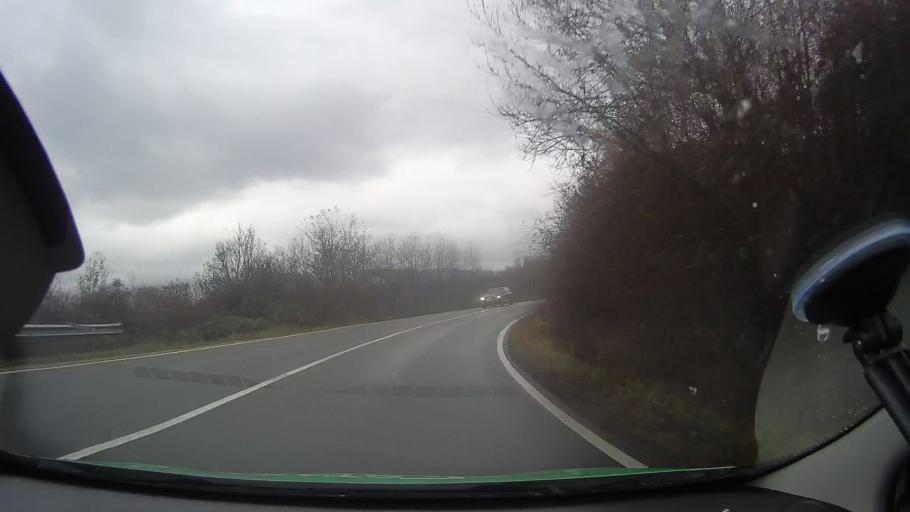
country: RO
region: Arad
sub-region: Comuna Almas
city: Almas
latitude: 46.2989
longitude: 22.2039
